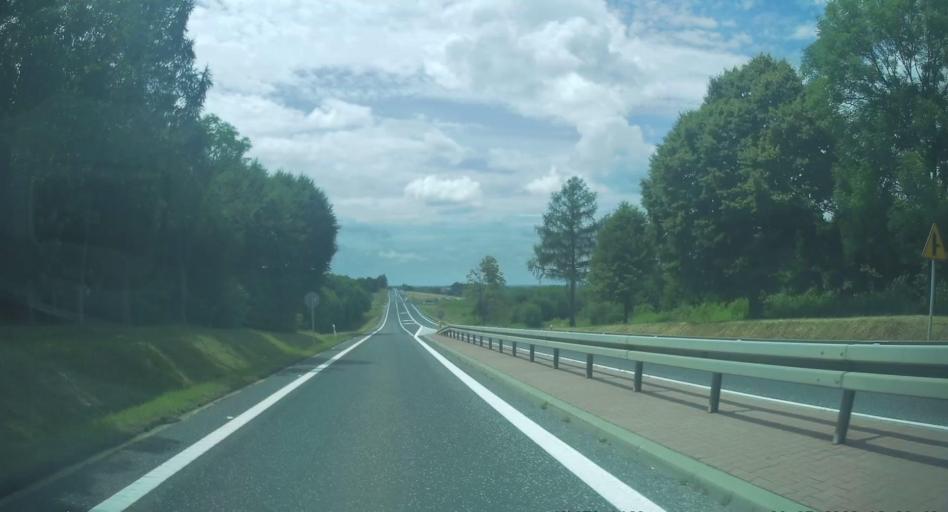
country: PL
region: Subcarpathian Voivodeship
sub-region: Powiat ropczycko-sedziszowski
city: Ropczyce
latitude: 50.0617
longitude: 21.5660
